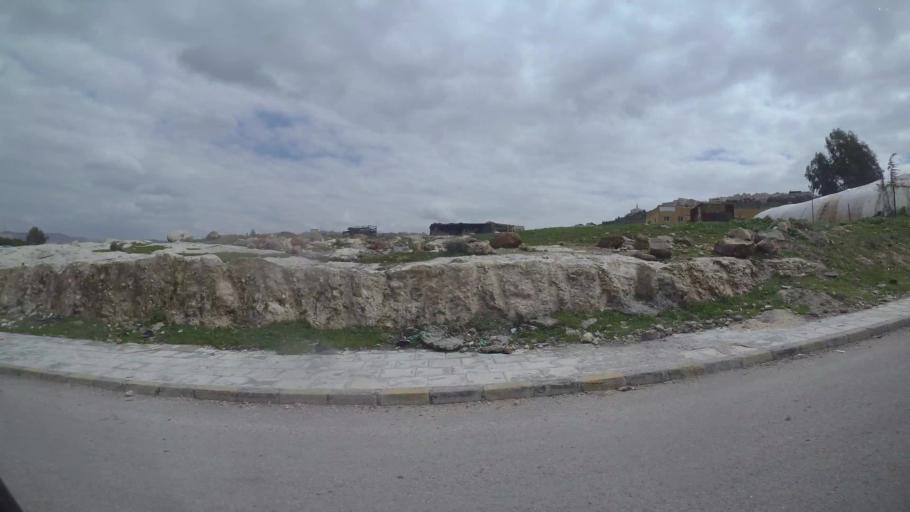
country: JO
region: Amman
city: Al Jubayhah
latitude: 32.0502
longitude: 35.8331
